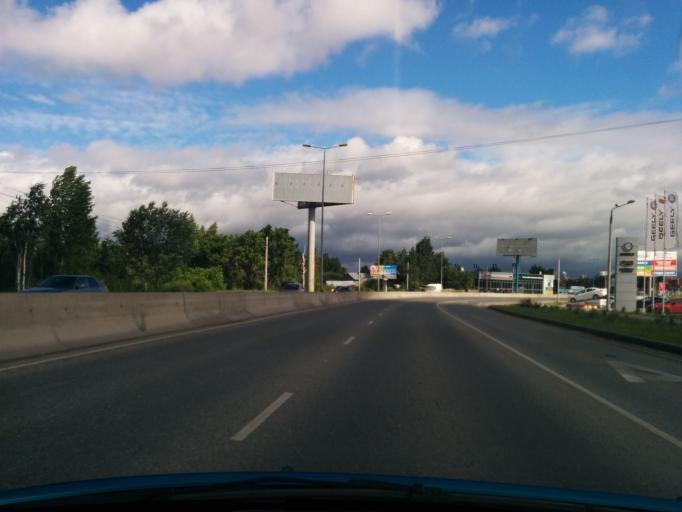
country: RU
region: Perm
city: Perm
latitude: 58.0303
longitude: 56.2150
